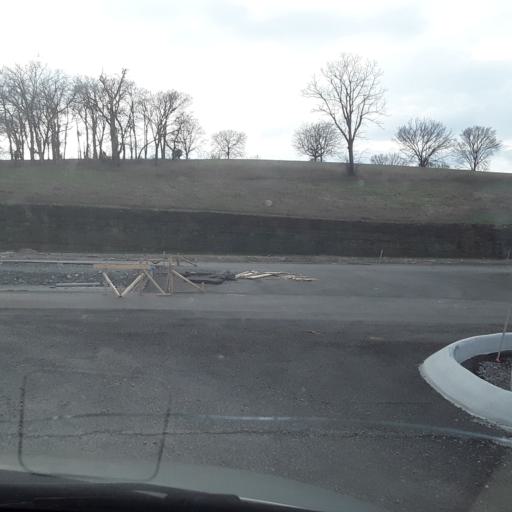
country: US
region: Tennessee
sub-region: Wilson County
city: Lebanon
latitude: 36.2322
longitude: -86.3697
